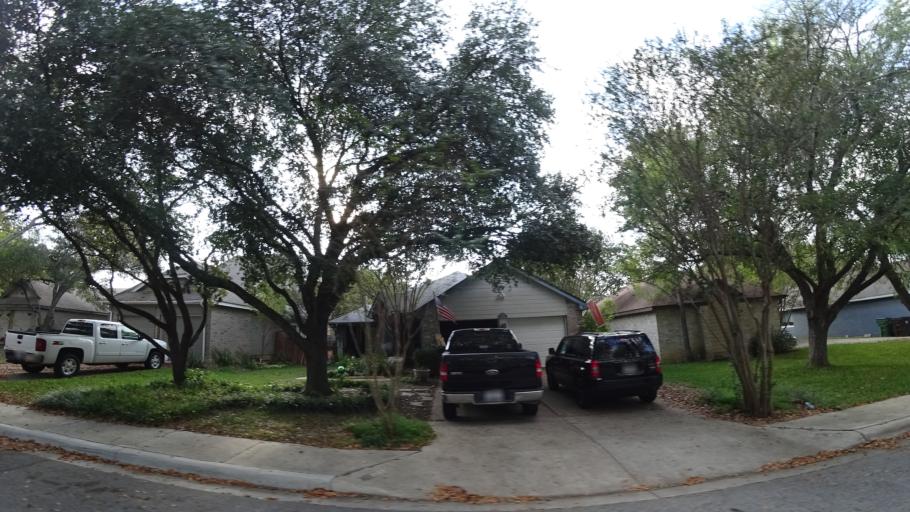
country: US
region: Texas
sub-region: Williamson County
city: Round Rock
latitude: 30.4929
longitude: -97.6657
